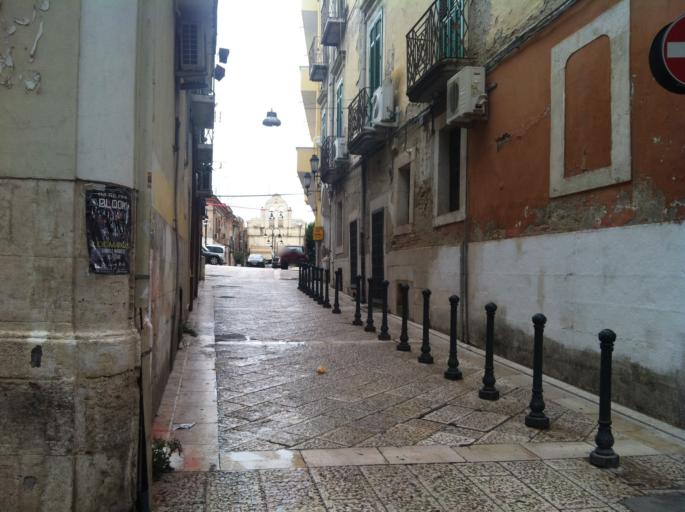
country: IT
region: Apulia
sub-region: Provincia di Foggia
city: Foggia
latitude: 41.4643
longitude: 15.5437
